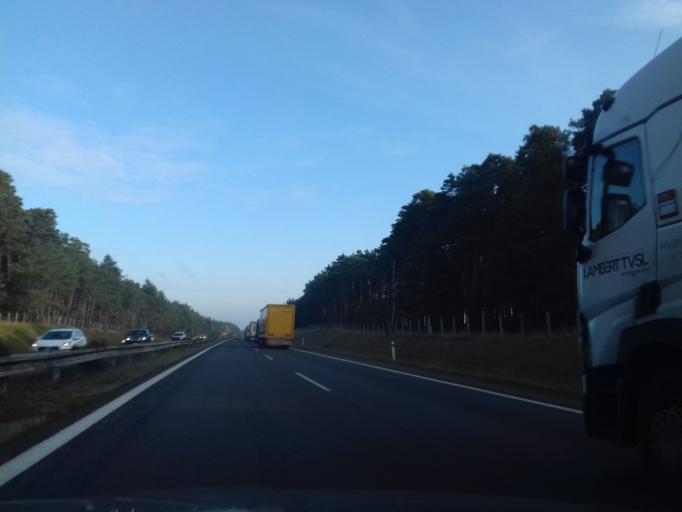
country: SK
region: Bratislavsky
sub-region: Okres Malacky
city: Malacky
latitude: 48.3989
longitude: 17.0288
